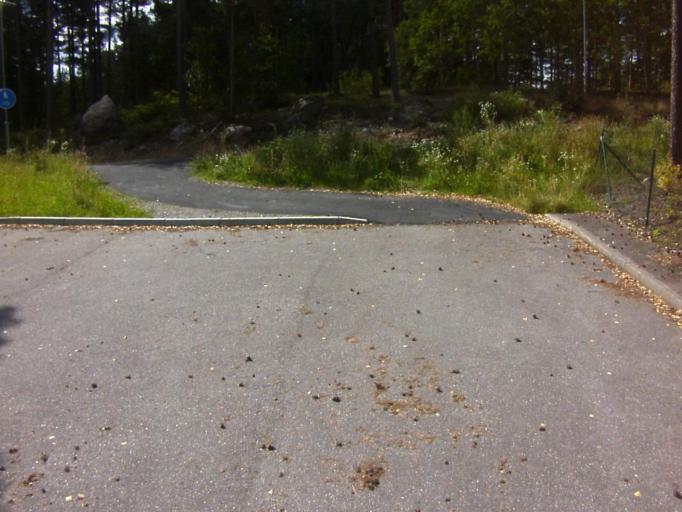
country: SE
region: Soedermanland
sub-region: Eskilstuna Kommun
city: Hallbybrunn
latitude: 59.3463
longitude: 16.4349
